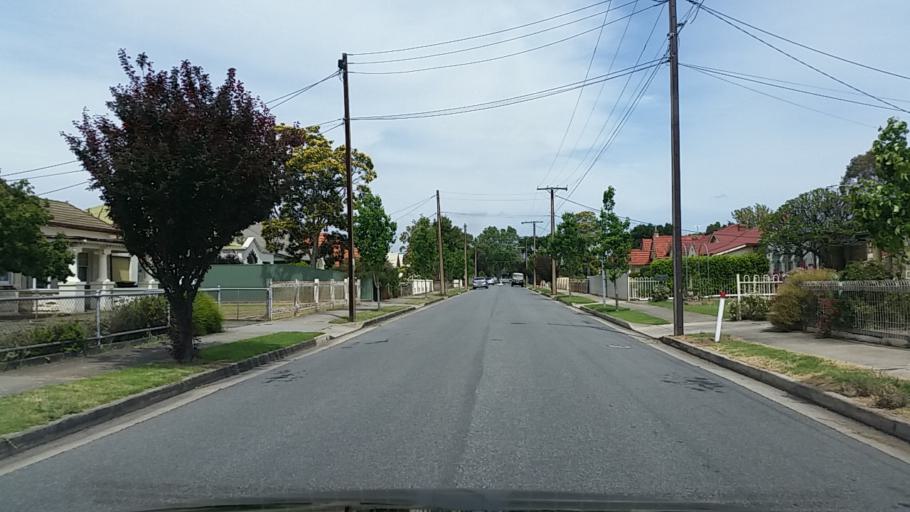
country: AU
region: South Australia
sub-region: Charles Sturt
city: Woodville
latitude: -34.8867
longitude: 138.5587
